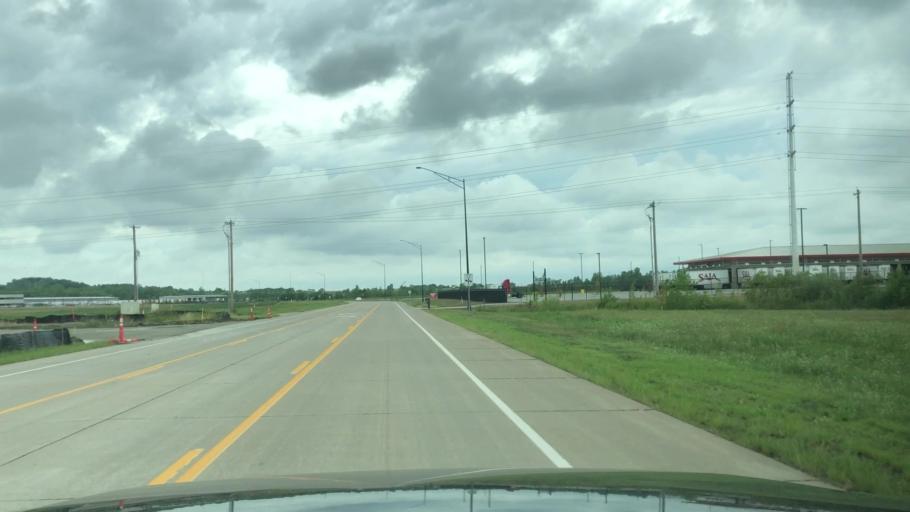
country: US
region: Missouri
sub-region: Saint Charles County
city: Saint Peters
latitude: 38.8107
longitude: -90.5752
